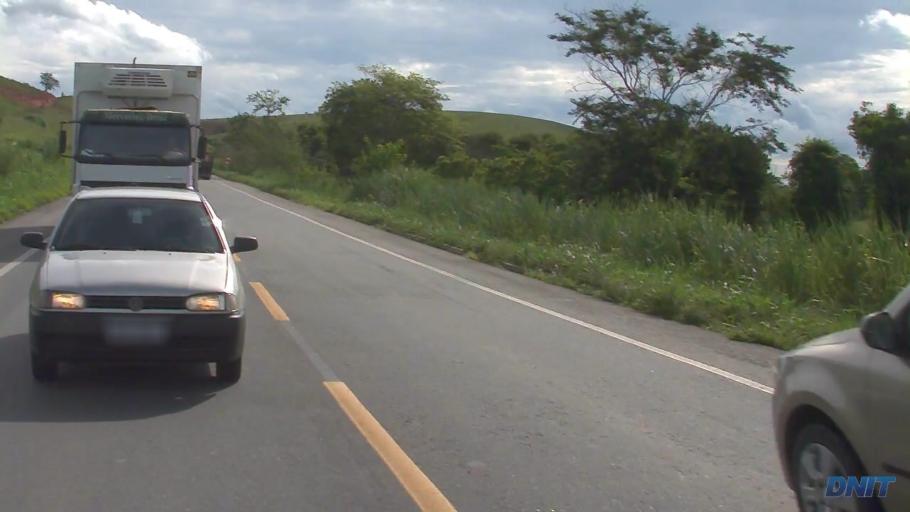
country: BR
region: Minas Gerais
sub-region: Belo Oriente
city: Belo Oriente
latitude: -19.2133
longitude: -42.3065
